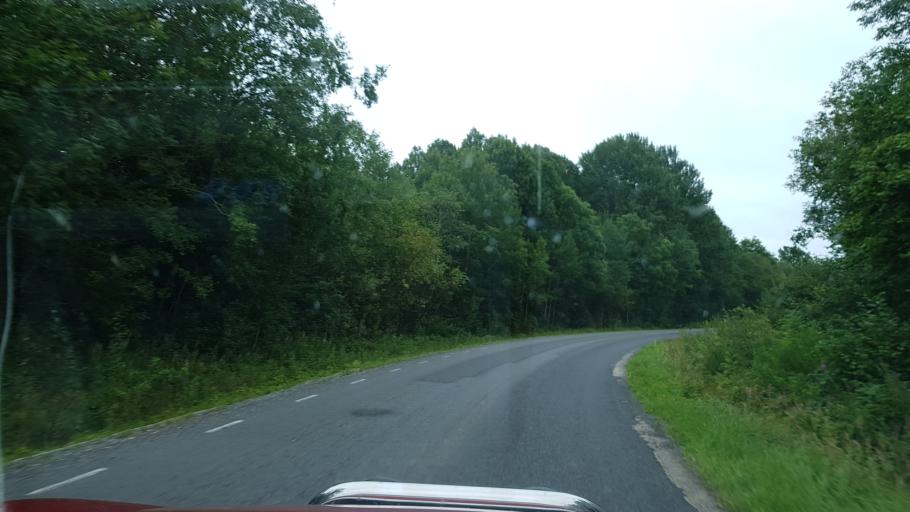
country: EE
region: Laeaene
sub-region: Lihula vald
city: Lihula
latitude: 58.8766
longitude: 23.8760
